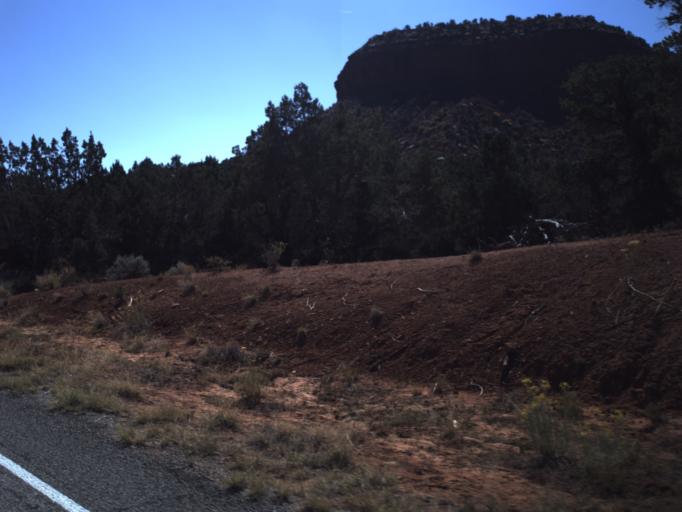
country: US
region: Utah
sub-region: San Juan County
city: Blanding
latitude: 37.5669
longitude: -110.0321
